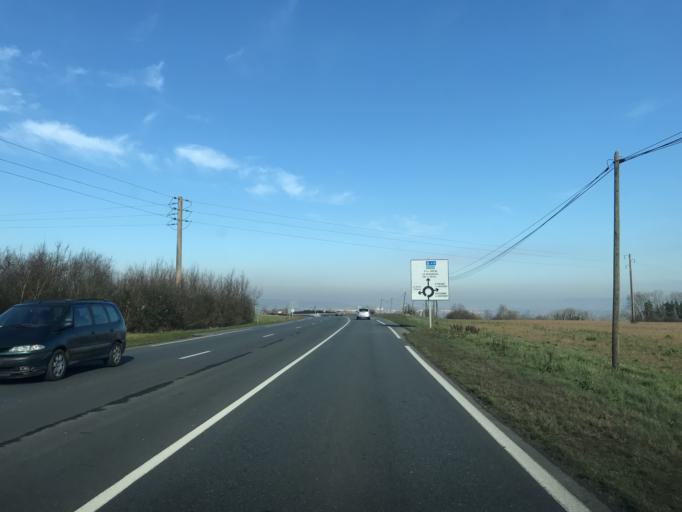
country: FR
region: Haute-Normandie
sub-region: Departement de l'Eure
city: Saint-Pierre-du-Vauvray
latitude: 49.2243
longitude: 1.2127
